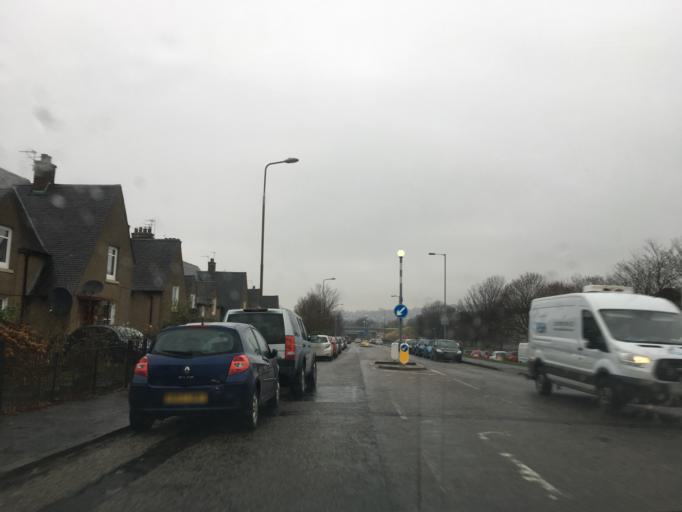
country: GB
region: Scotland
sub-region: Edinburgh
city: Colinton
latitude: 55.9297
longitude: -3.2727
